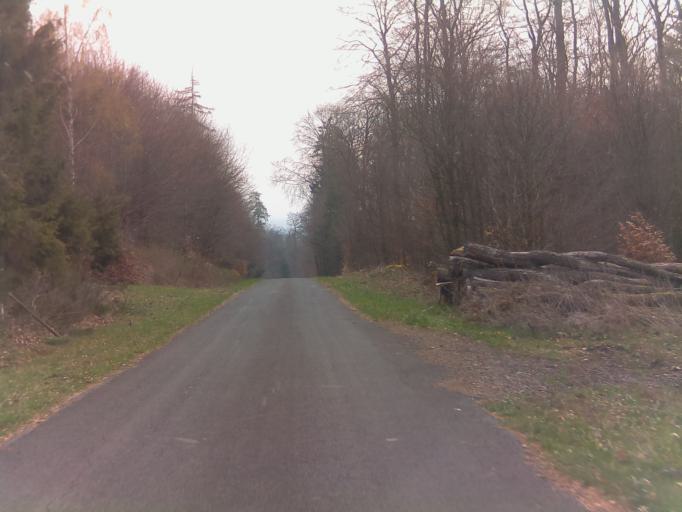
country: DE
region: Rheinland-Pfalz
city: Hattgenstein
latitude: 49.7158
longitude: 7.1636
